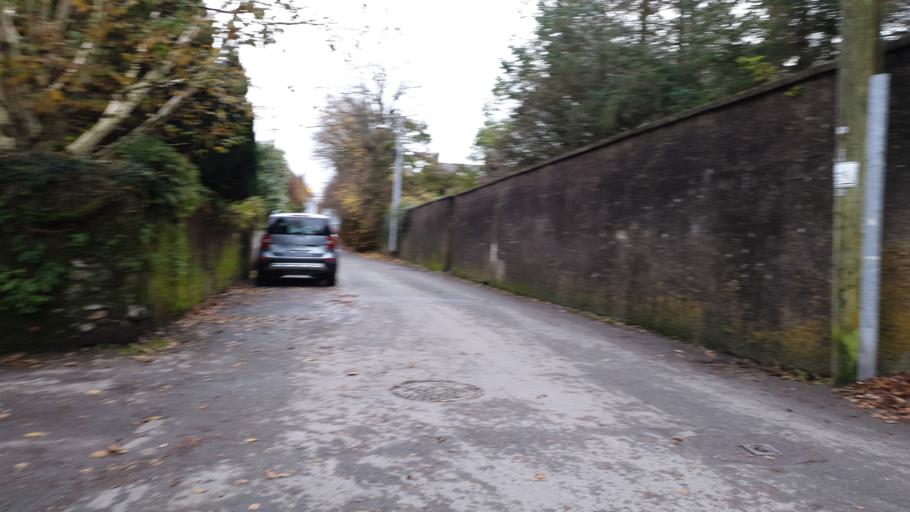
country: IE
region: Munster
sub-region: County Cork
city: Cork
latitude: 51.8976
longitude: -8.4286
